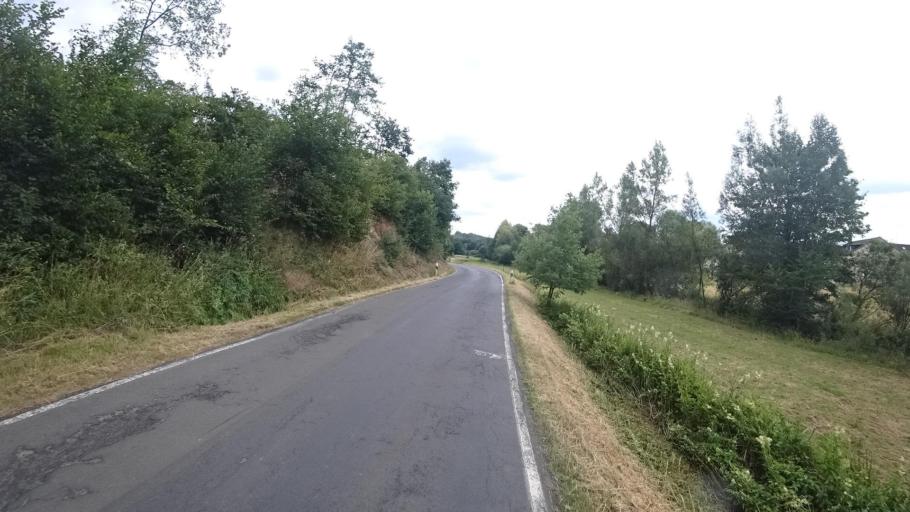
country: DE
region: Rheinland-Pfalz
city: Hemmelzen
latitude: 50.6891
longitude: 7.5805
